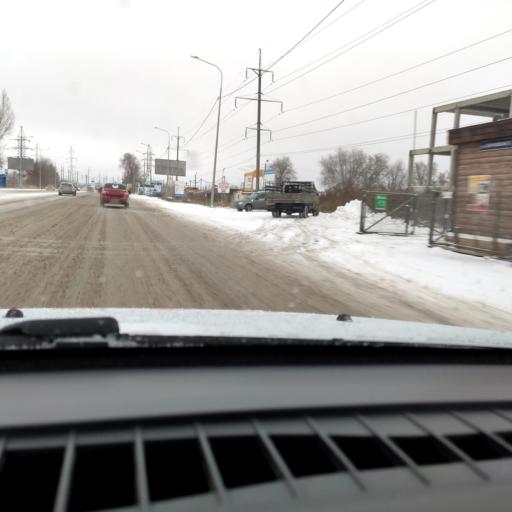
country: RU
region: Samara
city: Tol'yatti
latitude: 53.5752
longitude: 49.2931
